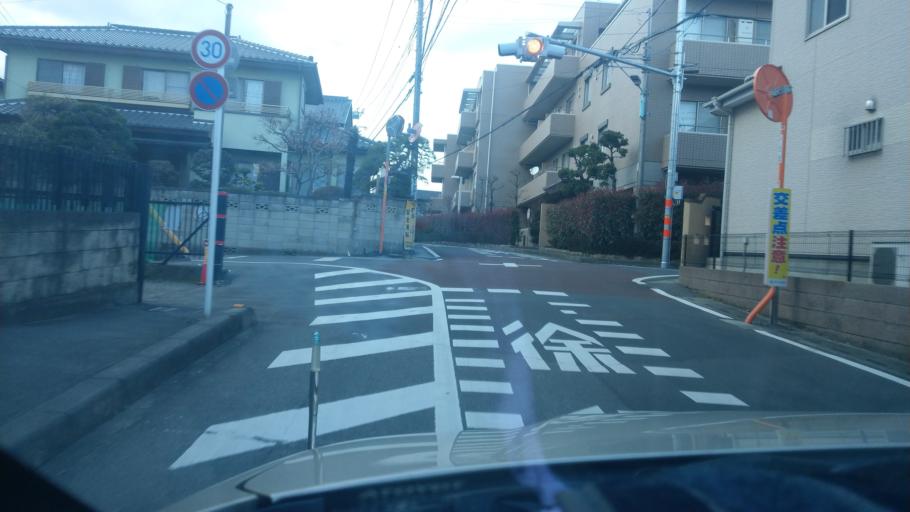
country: JP
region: Saitama
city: Yono
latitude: 35.8968
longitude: 139.5999
